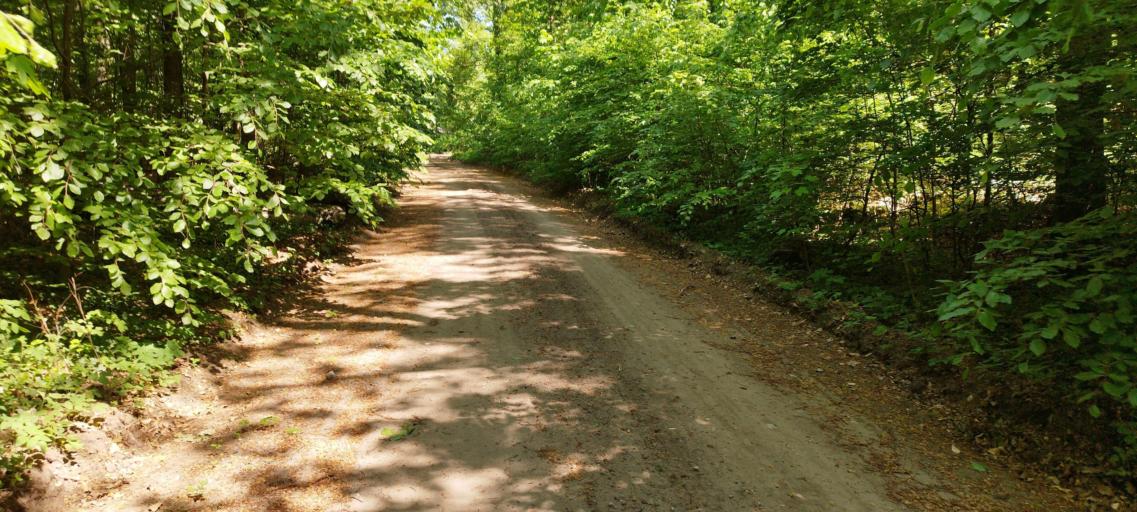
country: DE
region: Brandenburg
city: Rauen
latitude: 52.3840
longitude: 14.0150
